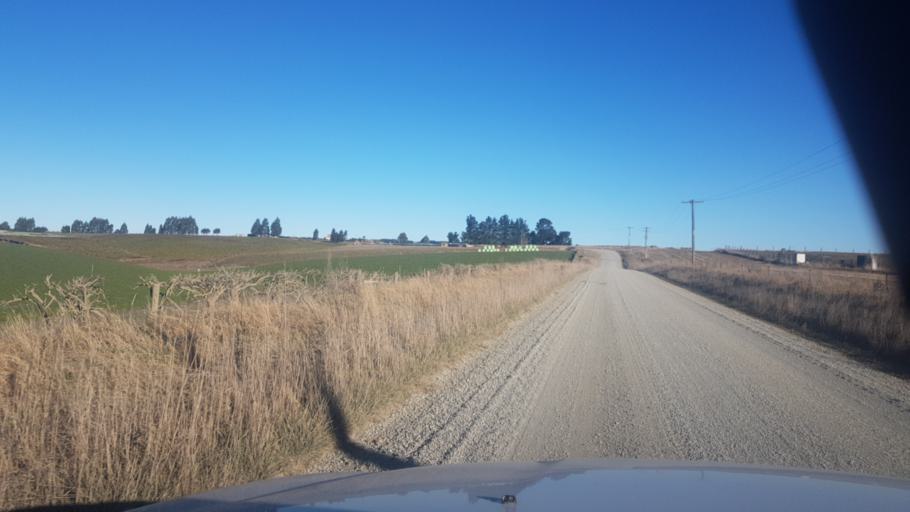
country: NZ
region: Canterbury
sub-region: Timaru District
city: Pleasant Point
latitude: -44.3541
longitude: 171.0703
